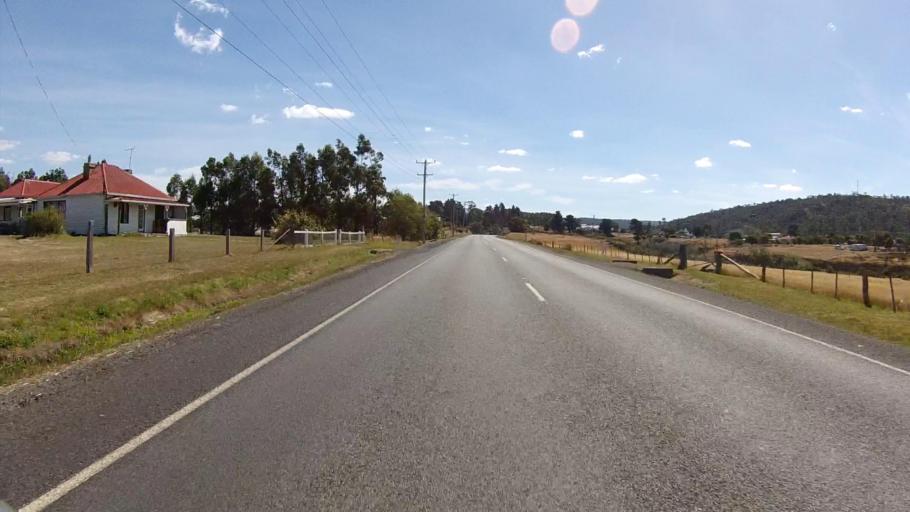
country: AU
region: Tasmania
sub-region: Sorell
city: Sorell
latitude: -42.6110
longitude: 147.7267
